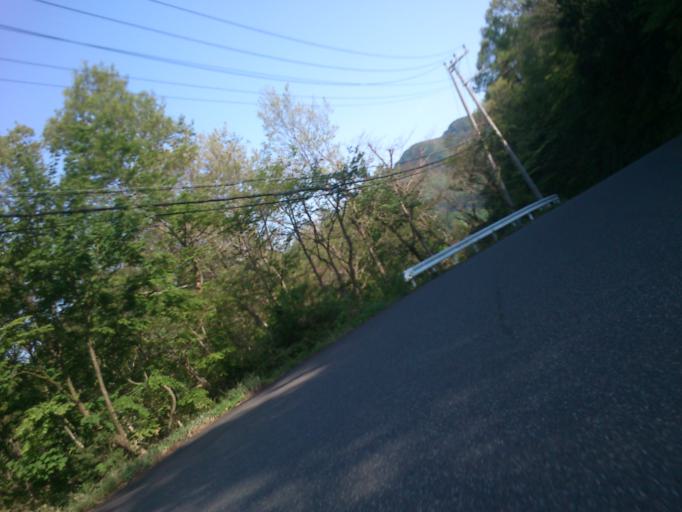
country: JP
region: Kyoto
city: Miyazu
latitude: 35.7076
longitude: 135.1906
